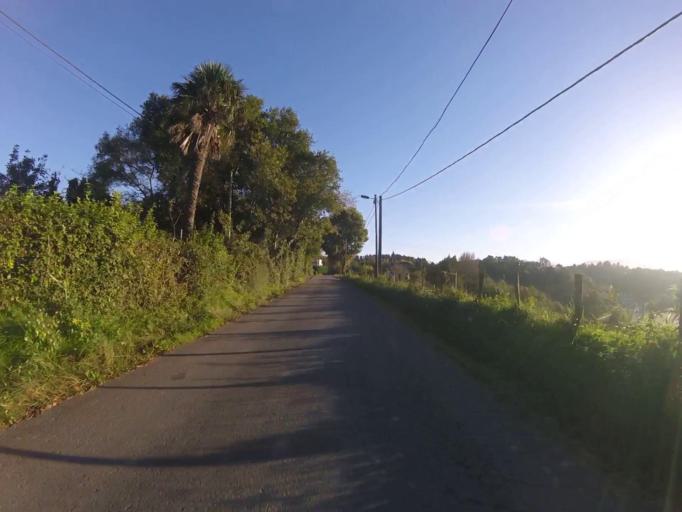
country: ES
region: Basque Country
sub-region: Provincia de Guipuzcoa
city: Lasarte
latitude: 43.2911
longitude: -2.0154
